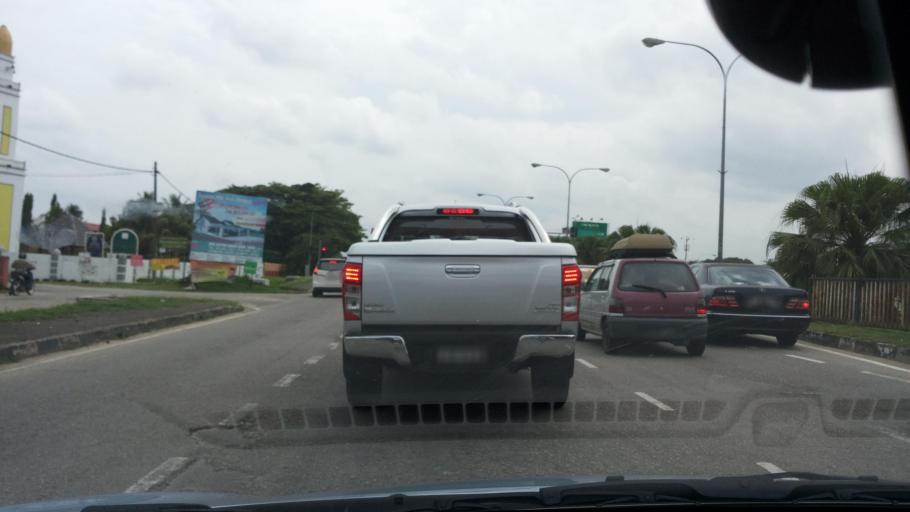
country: MY
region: Pahang
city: Kuantan
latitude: 3.7696
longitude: 103.2359
